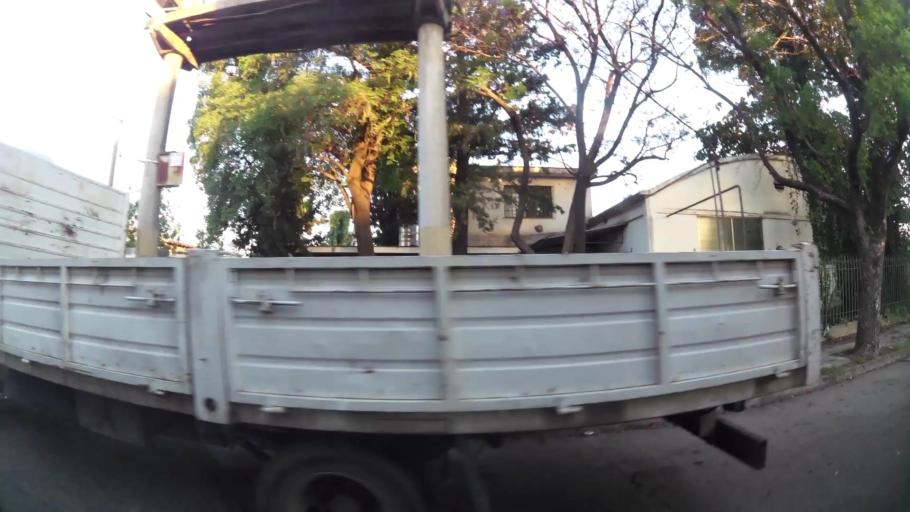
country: AR
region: Cordoba
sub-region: Departamento de Capital
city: Cordoba
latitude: -31.3800
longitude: -64.2189
